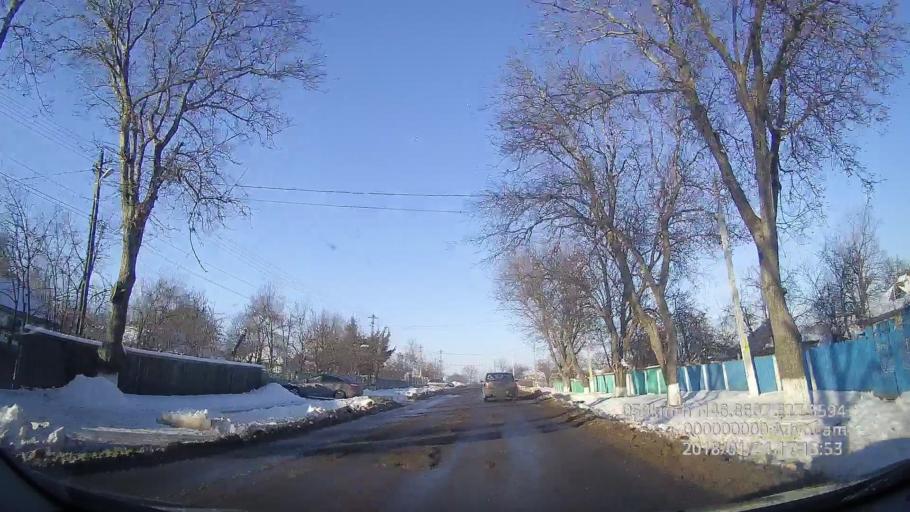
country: RO
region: Vaslui
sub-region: Comuna Rebricea
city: Rebricea
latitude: 46.8612
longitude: 27.5594
